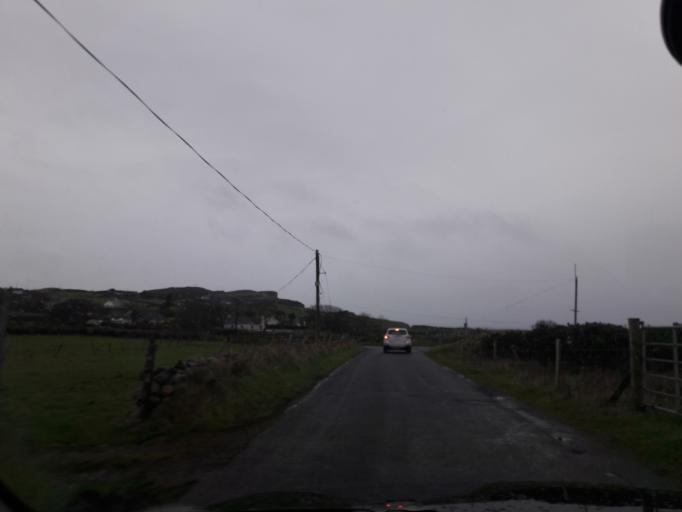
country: IE
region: Ulster
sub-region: County Donegal
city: Buncrana
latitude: 55.2472
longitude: -7.6221
